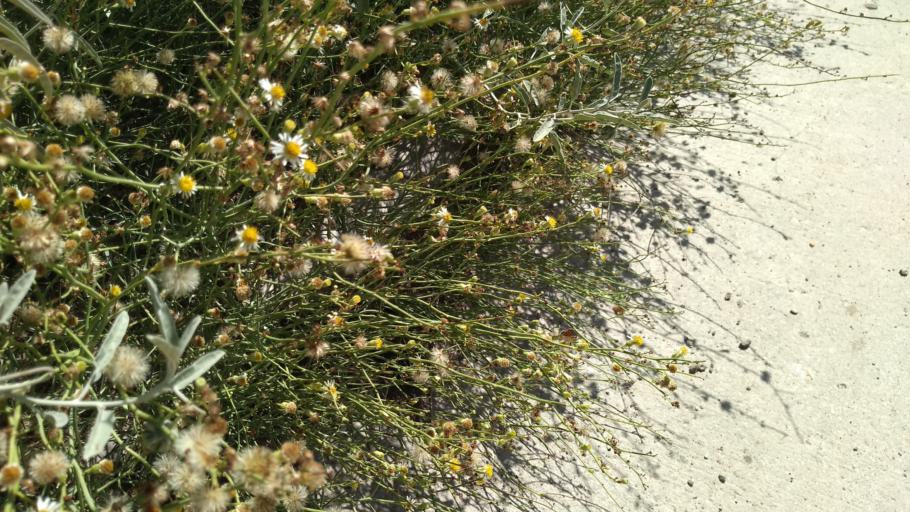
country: US
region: Texas
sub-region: El Paso County
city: El Paso
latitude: 31.7492
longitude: -106.4949
